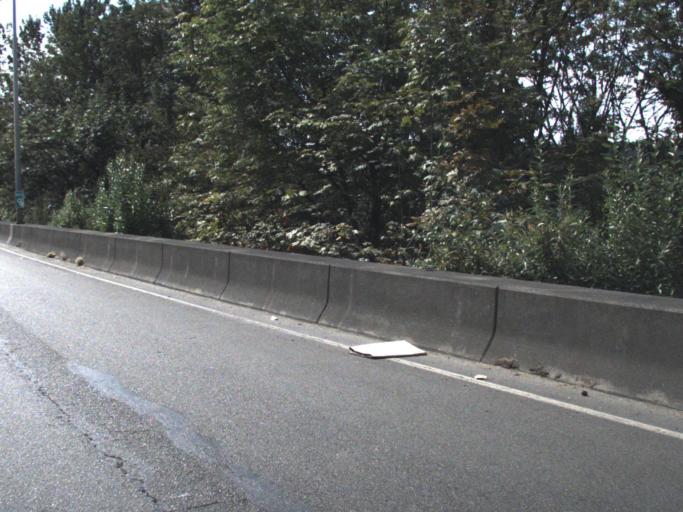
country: US
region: Washington
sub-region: King County
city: Newport
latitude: 47.5539
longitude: -122.1924
